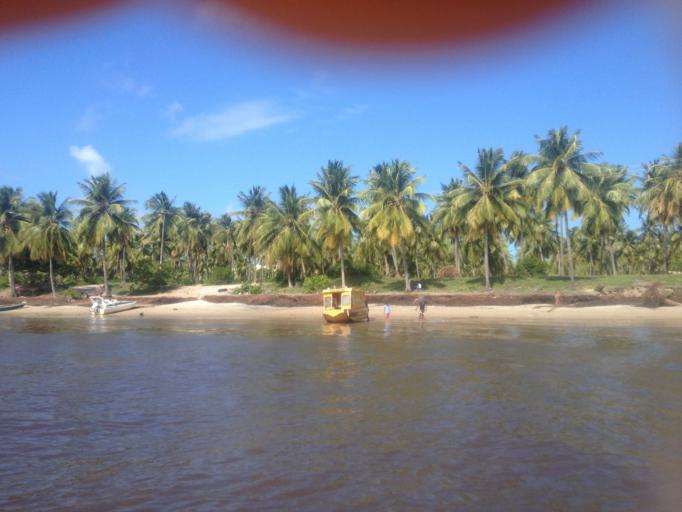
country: BR
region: Sergipe
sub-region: Indiaroba
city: Indiaroba
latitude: -11.4662
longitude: -37.3716
